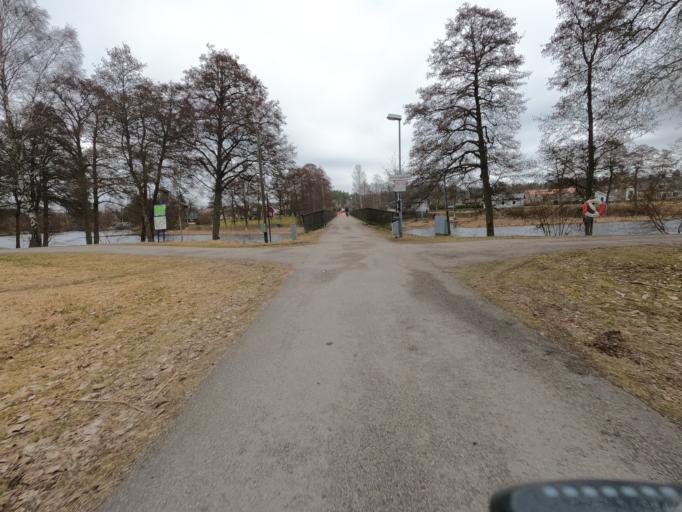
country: SE
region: Kronoberg
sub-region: Ljungby Kommun
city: Ljungby
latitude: 56.8357
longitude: 13.9629
